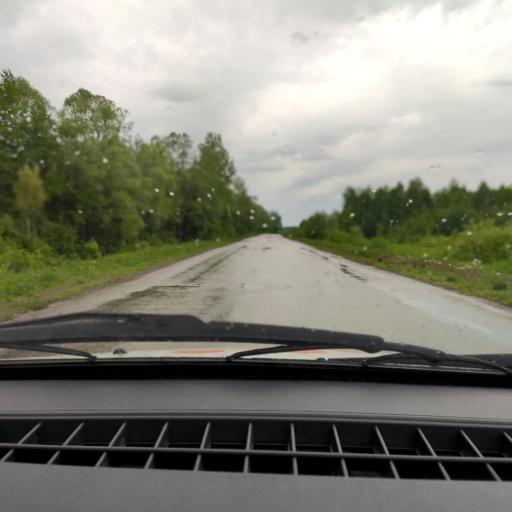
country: RU
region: Bashkortostan
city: Urman
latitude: 54.8613
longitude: 56.8375
